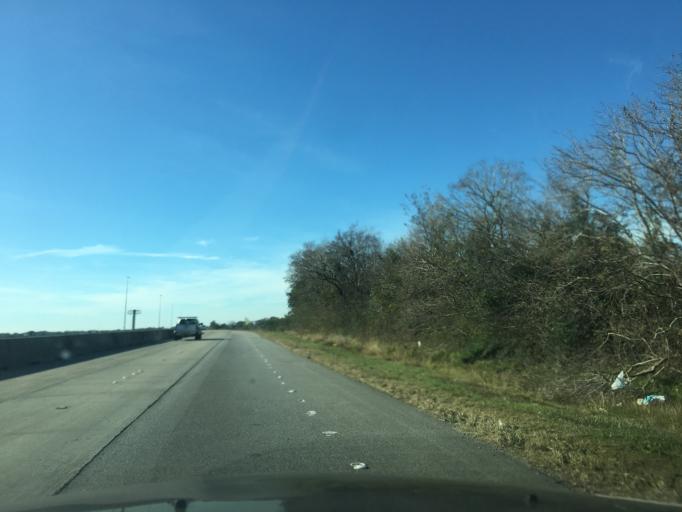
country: US
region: Texas
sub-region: Fort Bend County
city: Rosenberg
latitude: 29.5324
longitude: -95.8244
